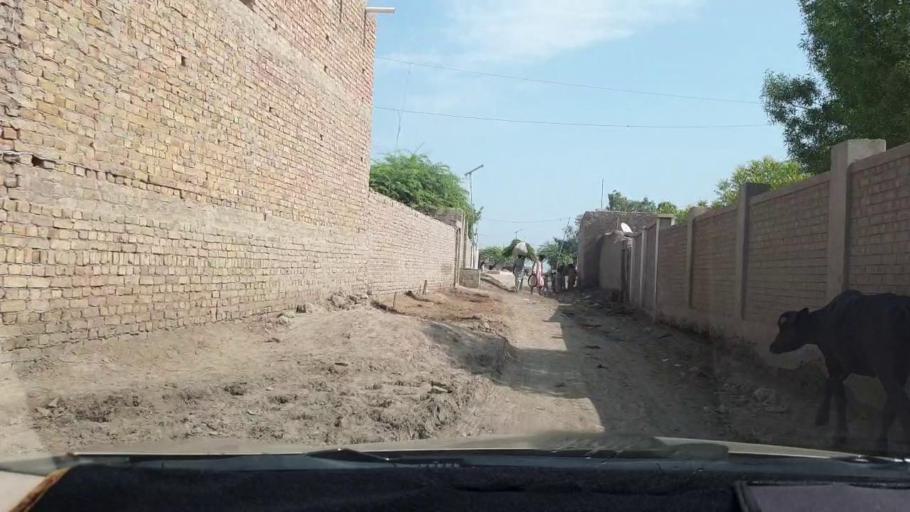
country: PK
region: Sindh
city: Larkana
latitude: 27.6661
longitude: 68.2227
